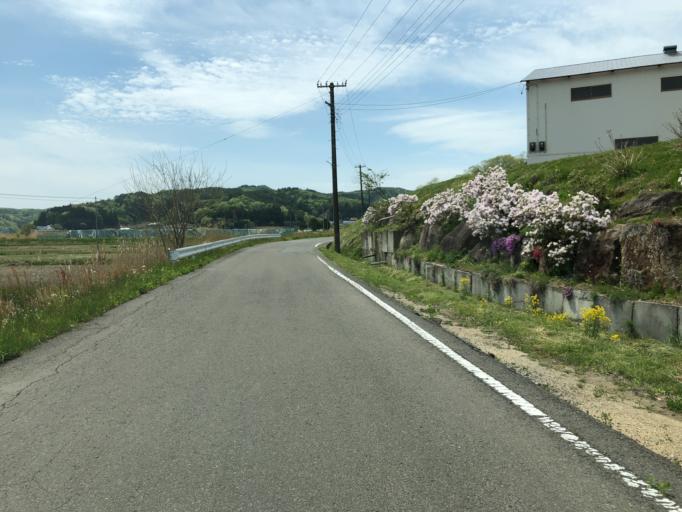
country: JP
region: Fukushima
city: Yanagawamachi-saiwaicho
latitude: 37.7193
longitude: 140.6994
